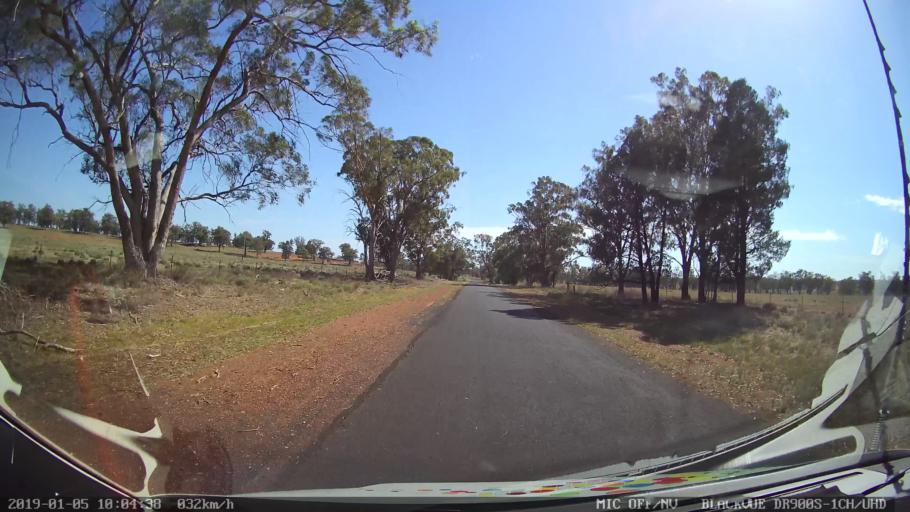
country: AU
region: New South Wales
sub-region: Gilgandra
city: Gilgandra
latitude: -31.6727
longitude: 148.8611
